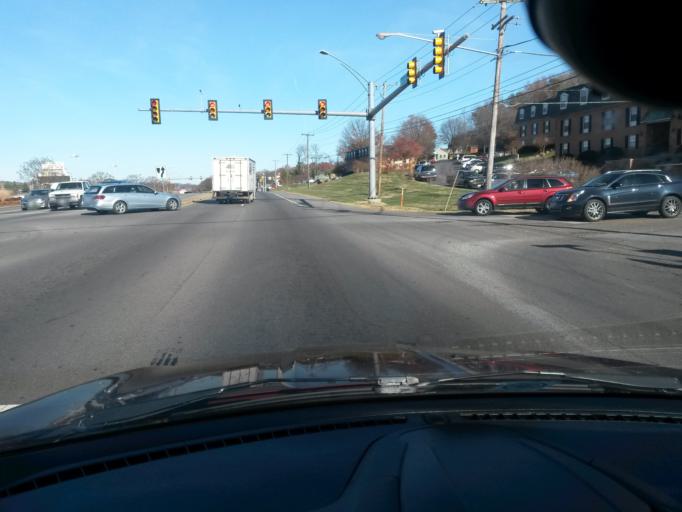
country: US
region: Virginia
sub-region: Roanoke County
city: Narrows
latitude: 37.2280
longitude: -79.9781
